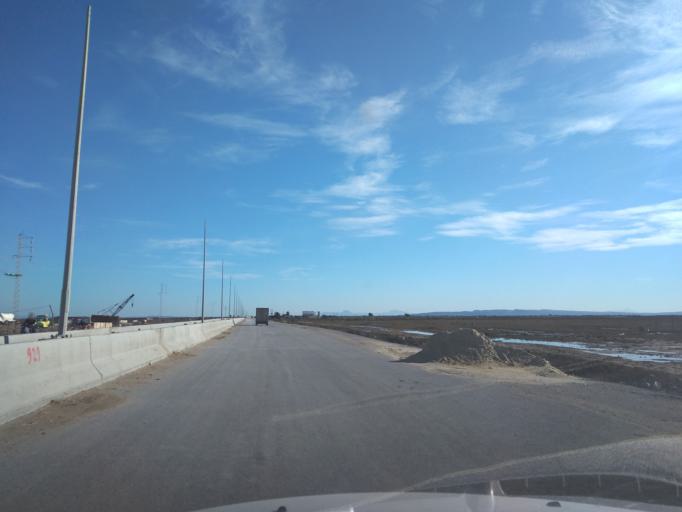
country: TN
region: Ariana
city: Qal'at al Andalus
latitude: 37.0467
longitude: 10.1254
